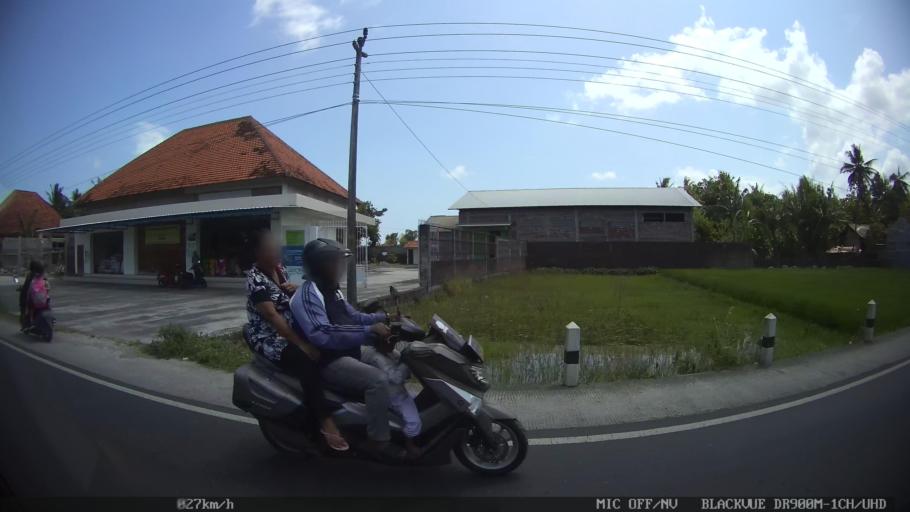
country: ID
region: Daerah Istimewa Yogyakarta
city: Pundong
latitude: -7.9258
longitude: 110.3734
